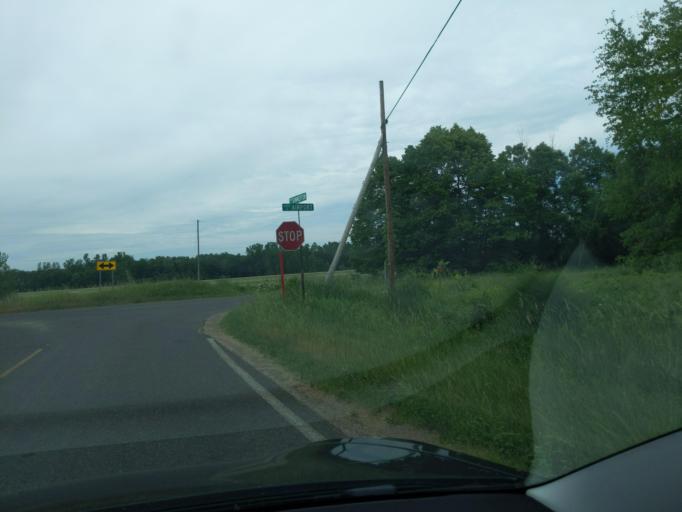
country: US
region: Michigan
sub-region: Isabella County
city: Mount Pleasant
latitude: 43.6187
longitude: -84.7278
